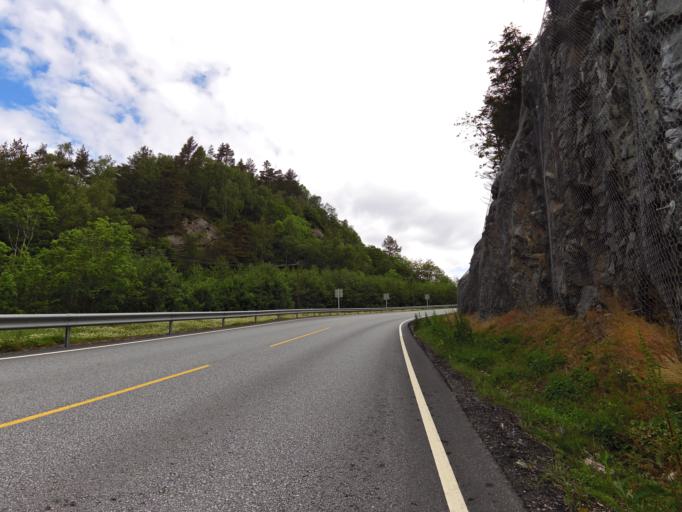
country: NO
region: Vest-Agder
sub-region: Lindesnes
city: Vigeland
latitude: 58.0540
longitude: 7.2109
